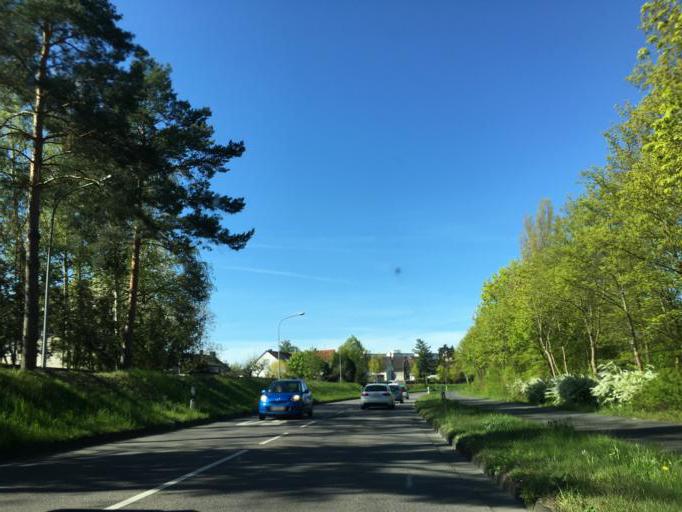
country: DE
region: Hesse
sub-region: Regierungsbezirk Darmstadt
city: Rodgau
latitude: 50.0049
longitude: 8.8720
